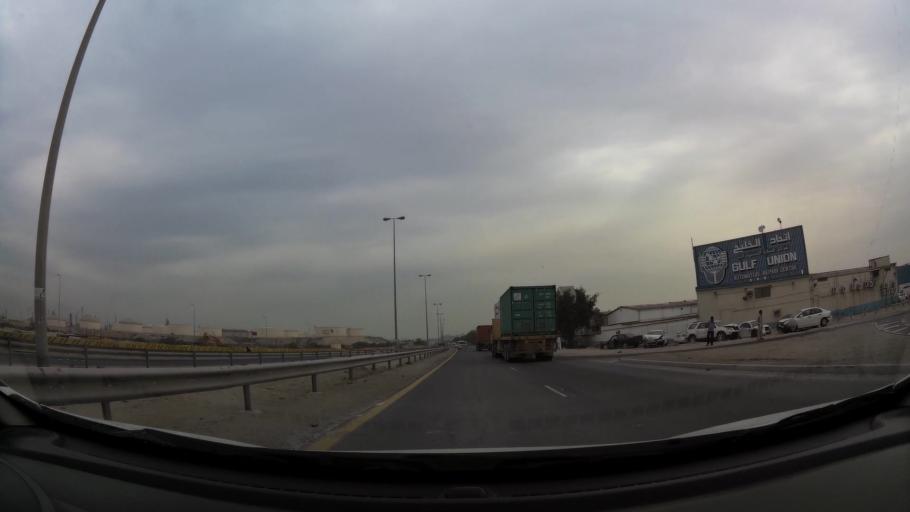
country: BH
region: Northern
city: Ar Rifa'
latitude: 26.1193
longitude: 50.5926
